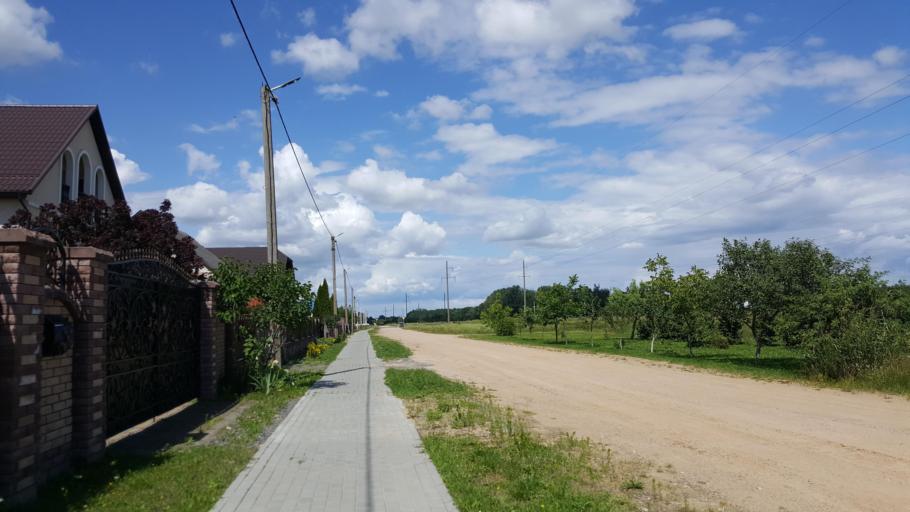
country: BY
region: Brest
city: Kamyanyets
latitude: 52.3932
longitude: 23.8157
